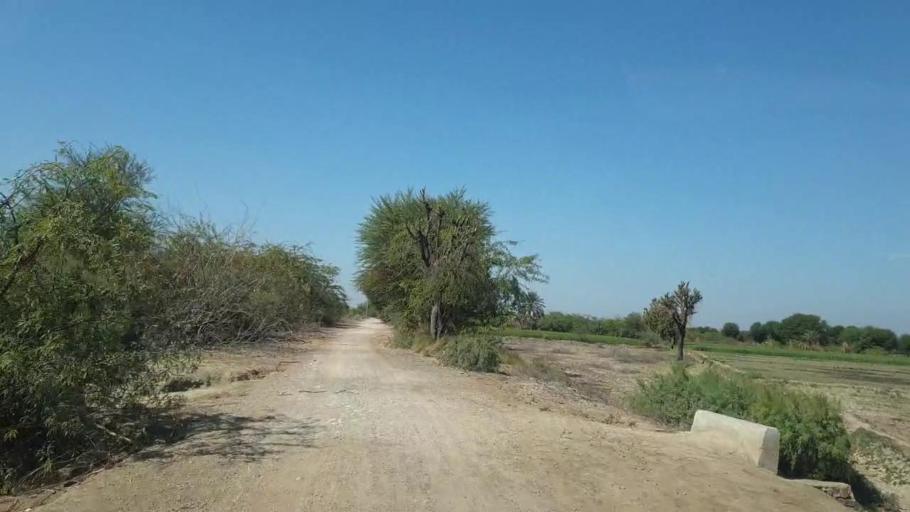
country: PK
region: Sindh
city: Mirpur Khas
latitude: 25.6141
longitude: 69.1386
